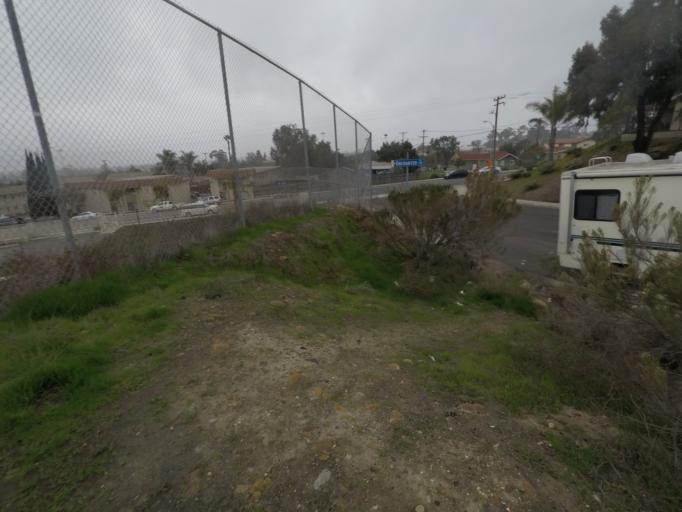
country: MX
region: Baja California
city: Tijuana
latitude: 32.5567
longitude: -117.0401
